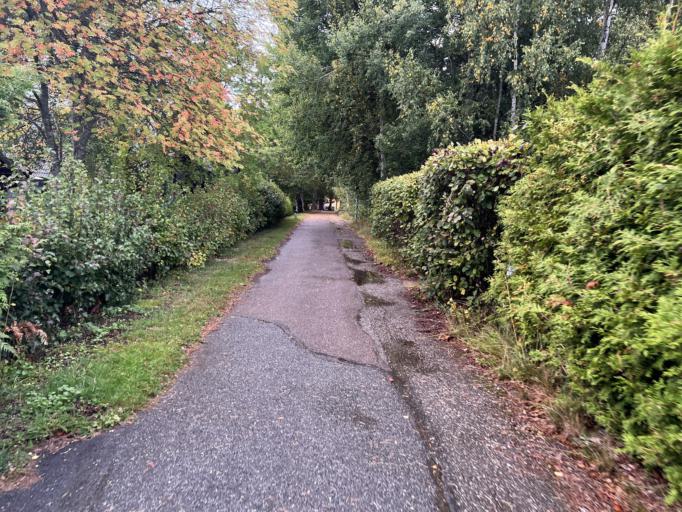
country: SE
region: Stockholm
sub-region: Vallentuna Kommun
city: Vallentuna
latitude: 59.4979
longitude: 18.0790
